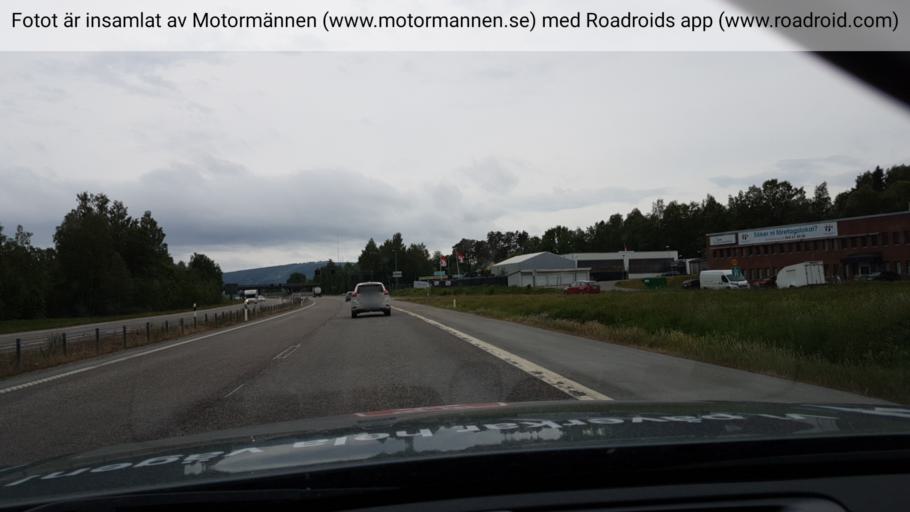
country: SE
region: Vaesternorrland
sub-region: Sundsvalls Kommun
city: Sundsvall
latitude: 62.4096
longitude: 17.3381
